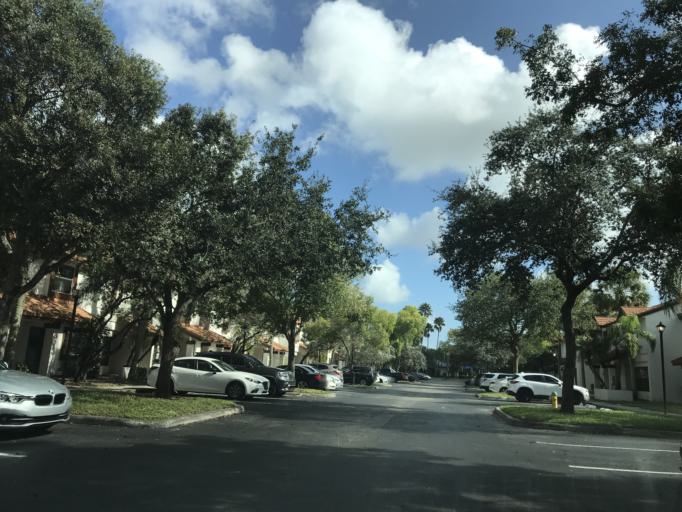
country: US
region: Florida
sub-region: Broward County
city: Coconut Creek
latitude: 26.2725
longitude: -80.1900
